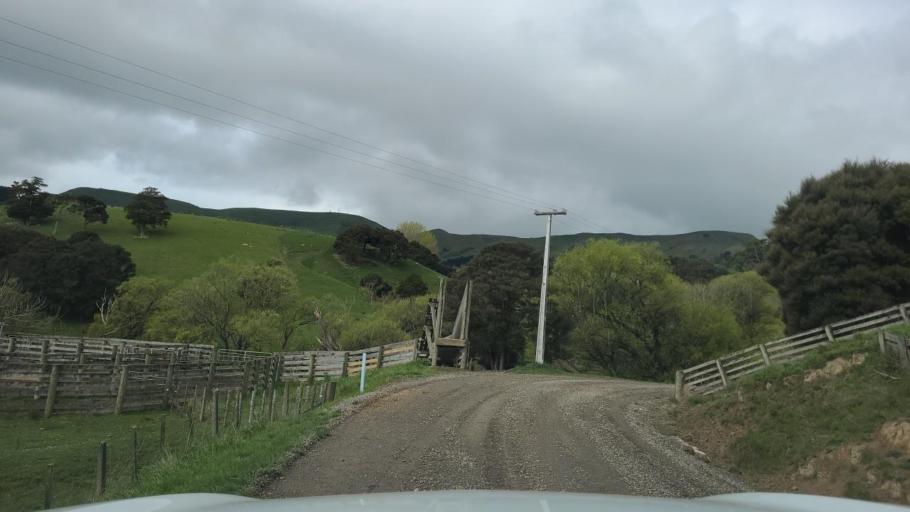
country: NZ
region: Wellington
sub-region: Masterton District
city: Masterton
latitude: -41.1720
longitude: 175.6274
